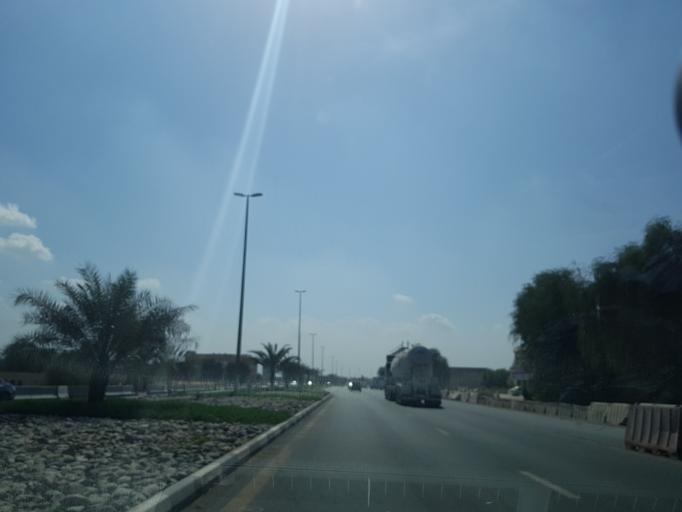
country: AE
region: Ra's al Khaymah
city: Ras al-Khaimah
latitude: 25.6964
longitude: 55.9671
